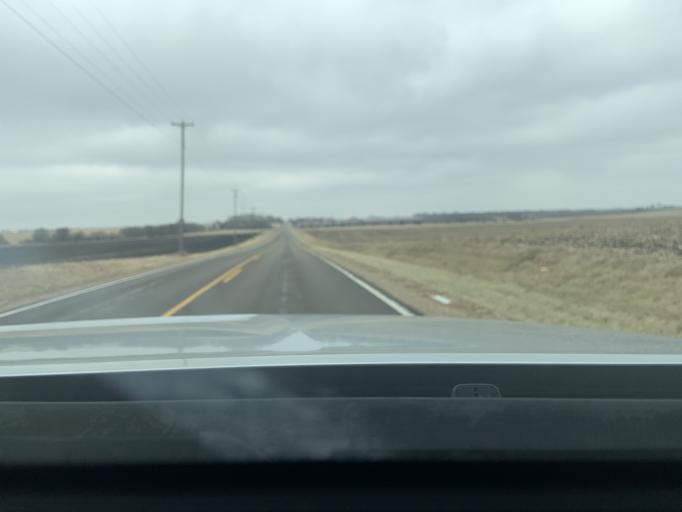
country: US
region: Illinois
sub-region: LaSalle County
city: Seneca
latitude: 41.3806
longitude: -88.6133
